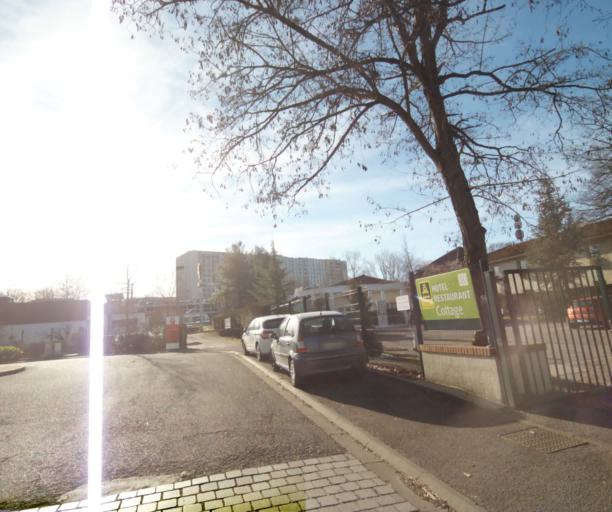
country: FR
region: Lorraine
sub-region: Departement de Meurthe-et-Moselle
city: Villers-les-Nancy
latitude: 48.6502
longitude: 6.1454
